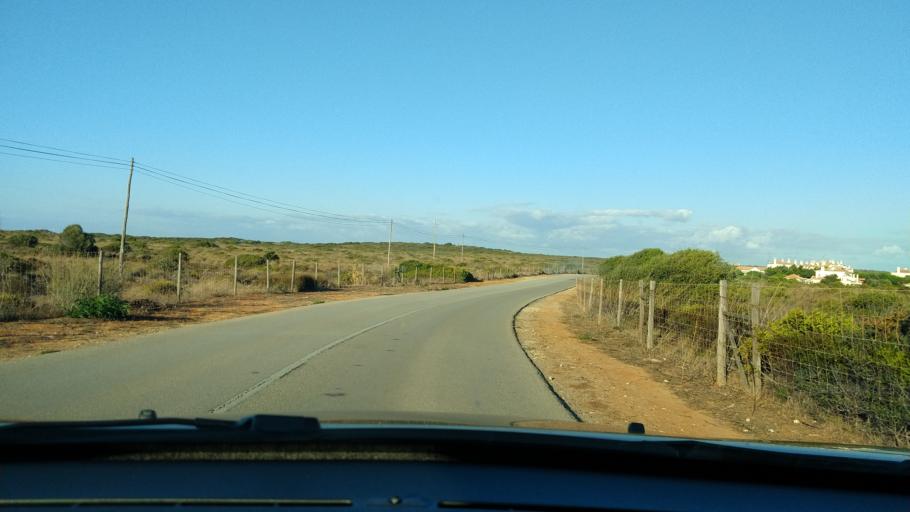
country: PT
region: Faro
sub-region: Vila do Bispo
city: Sagres
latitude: 37.0234
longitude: -8.9332
